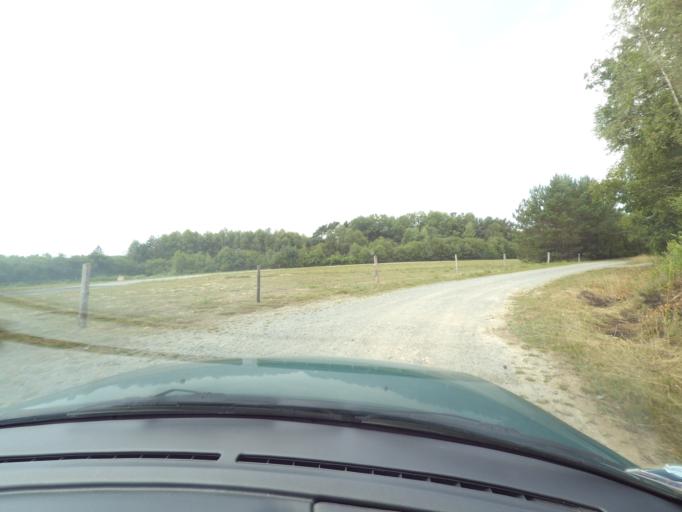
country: FR
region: Limousin
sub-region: Departement de la Correze
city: Bugeat
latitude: 45.7046
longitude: 2.0355
